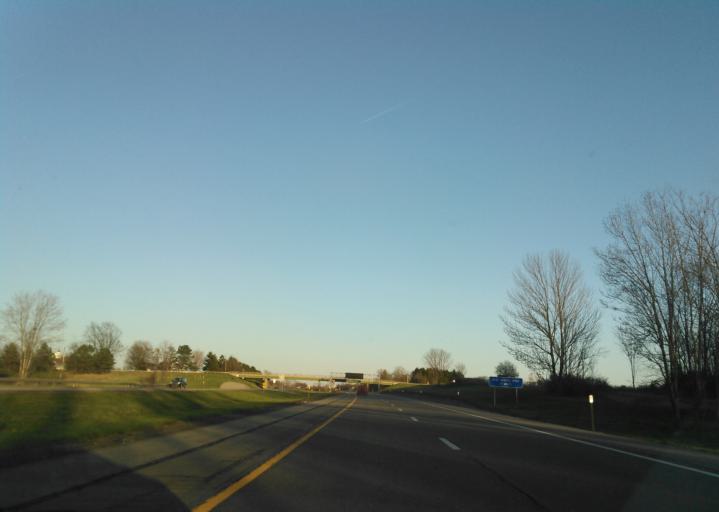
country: US
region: New York
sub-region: Monroe County
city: Pittsford
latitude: 43.0234
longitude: -77.5002
